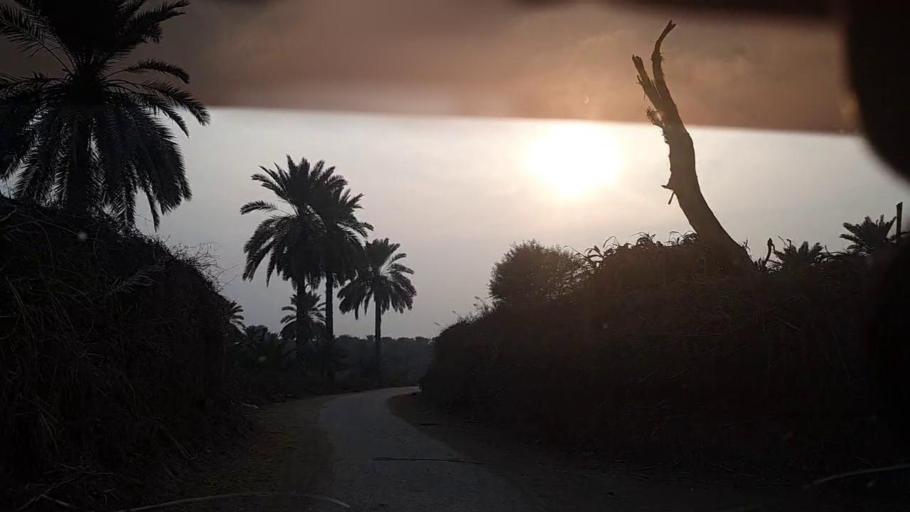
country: PK
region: Sindh
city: Khairpur
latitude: 27.4995
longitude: 68.6798
